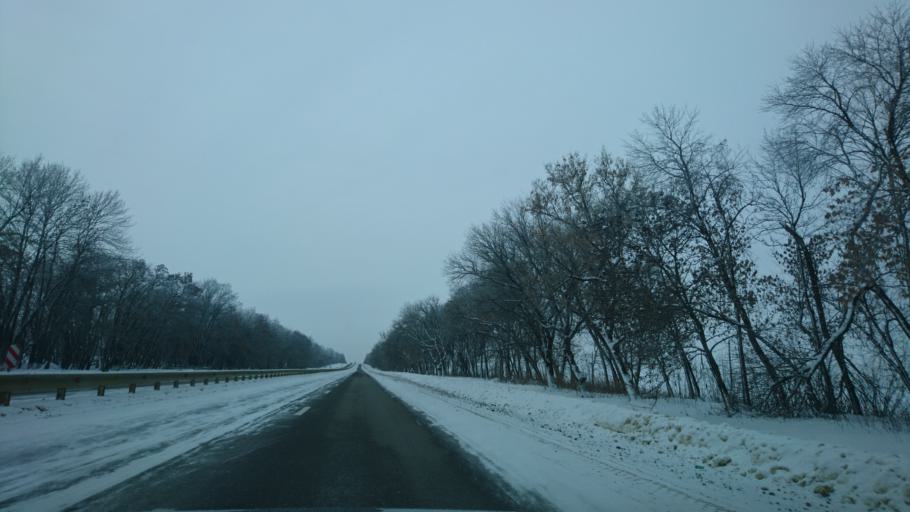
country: RU
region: Belgorod
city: Mayskiy
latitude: 50.4268
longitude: 36.3825
